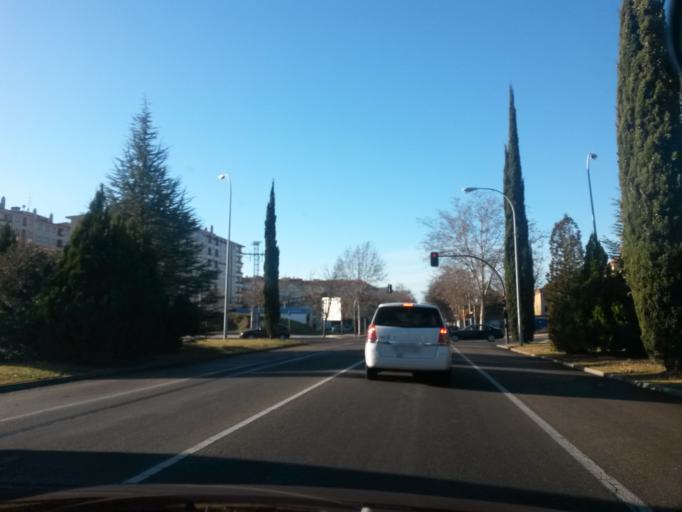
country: ES
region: Castille and Leon
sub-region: Provincia de Salamanca
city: Salamanca
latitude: 40.9797
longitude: -5.6574
